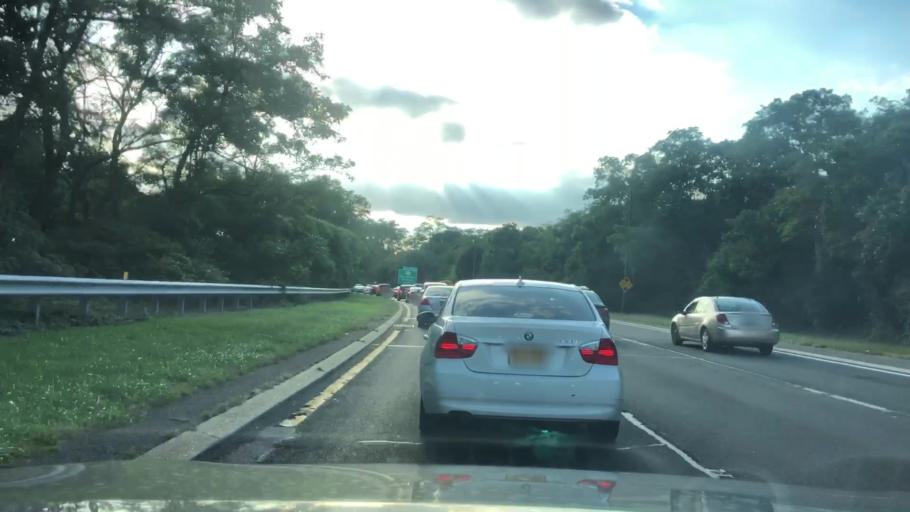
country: US
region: New York
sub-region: Nassau County
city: North Bellmore
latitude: 40.6999
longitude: -73.5307
